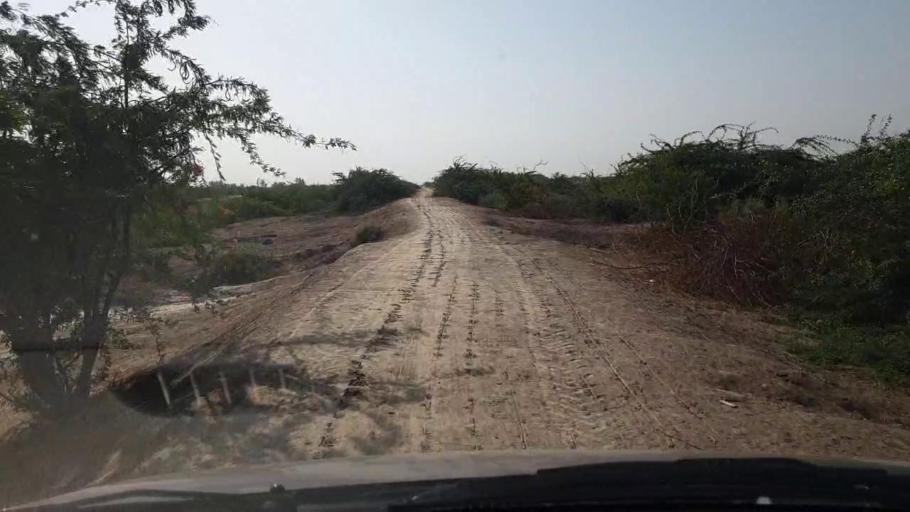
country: PK
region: Sindh
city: Kadhan
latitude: 24.5798
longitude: 69.0799
